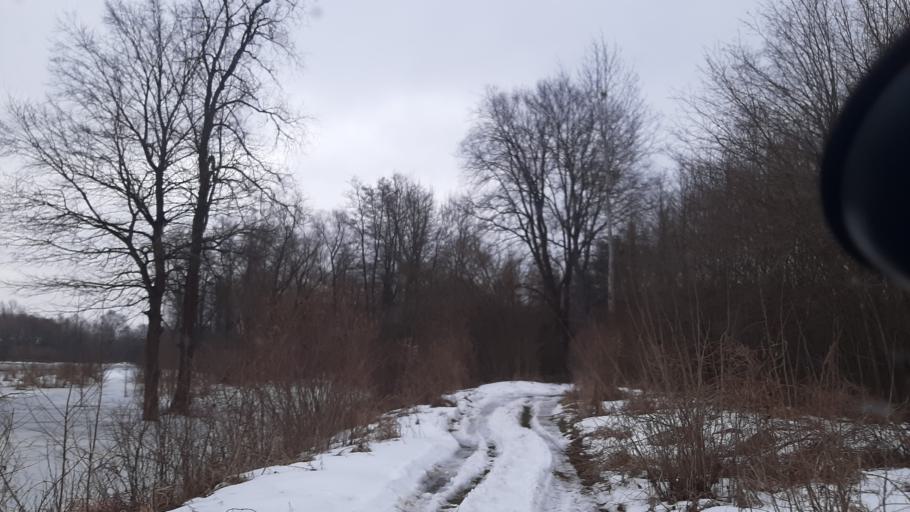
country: PL
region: Lublin Voivodeship
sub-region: Powiat wlodawski
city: Wlodawa
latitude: 51.5096
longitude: 23.6167
